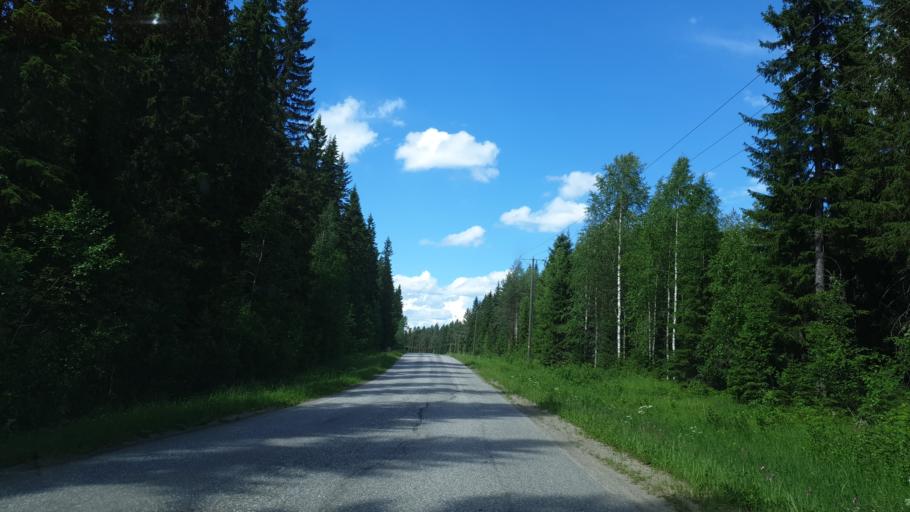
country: FI
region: Northern Savo
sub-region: Koillis-Savo
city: Kaavi
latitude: 63.0181
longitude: 28.6518
